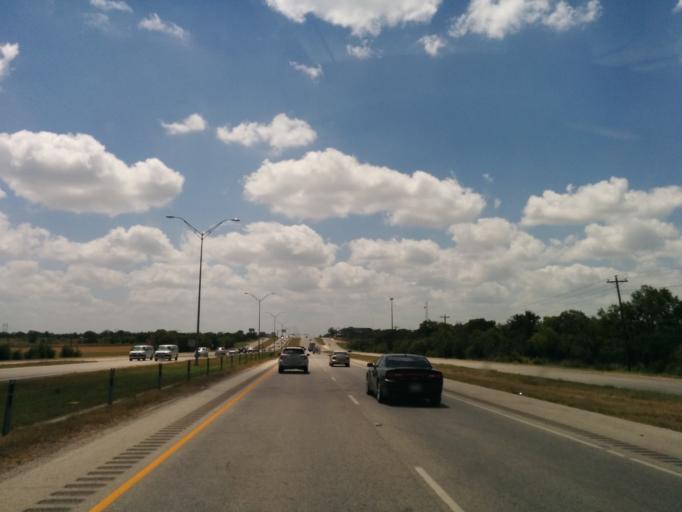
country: US
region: Texas
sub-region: Bastrop County
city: Bastrop
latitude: 30.1112
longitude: -97.3584
